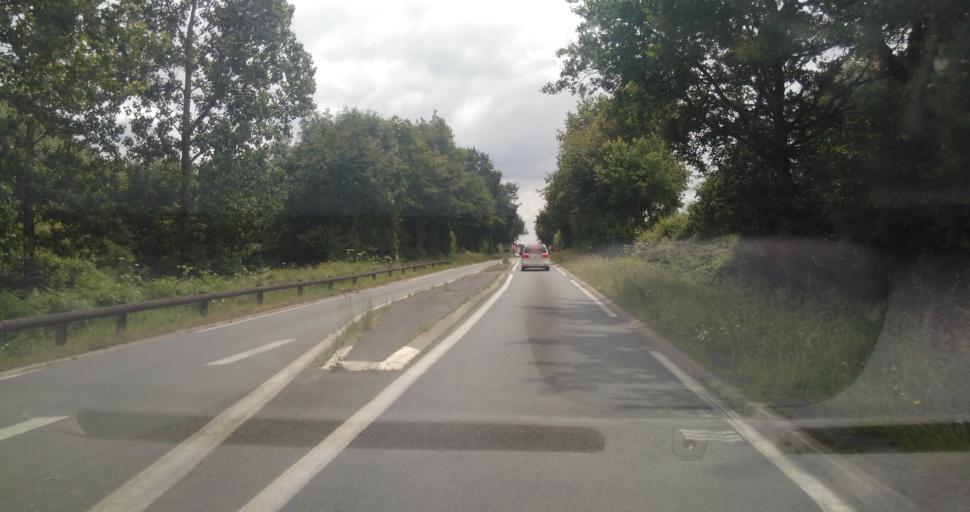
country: FR
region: Pays de la Loire
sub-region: Departement de la Vendee
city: Bournezeau
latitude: 46.6022
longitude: -1.1357
